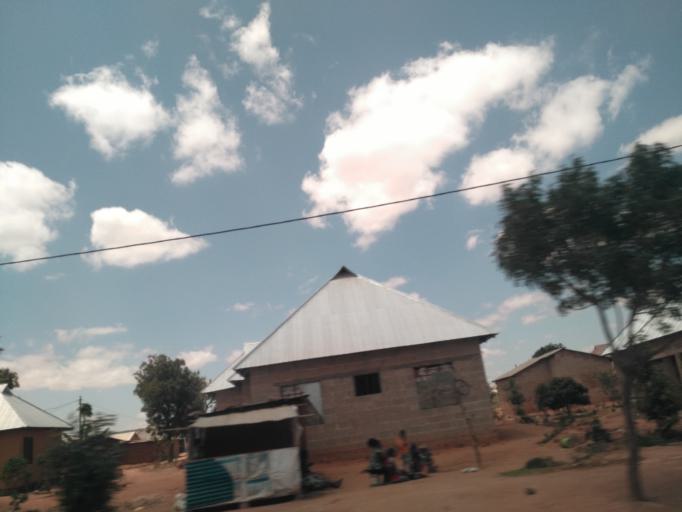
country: TZ
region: Dodoma
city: Kisasa
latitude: -6.1811
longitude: 35.7870
